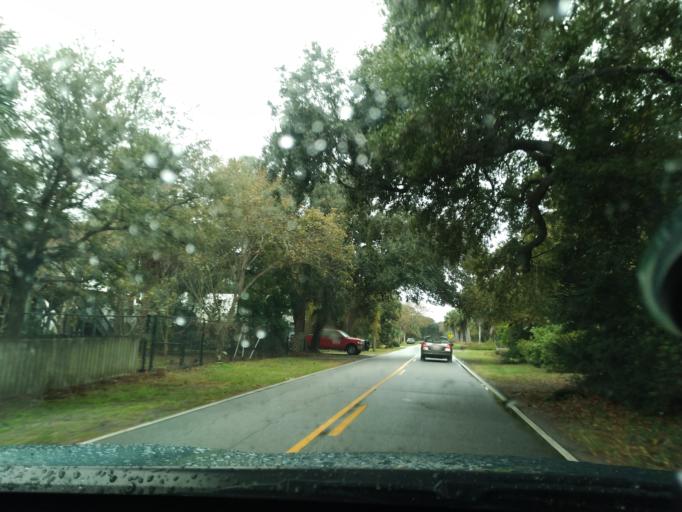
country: US
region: South Carolina
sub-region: Charleston County
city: Folly Beach
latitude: 32.6620
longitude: -79.9257
